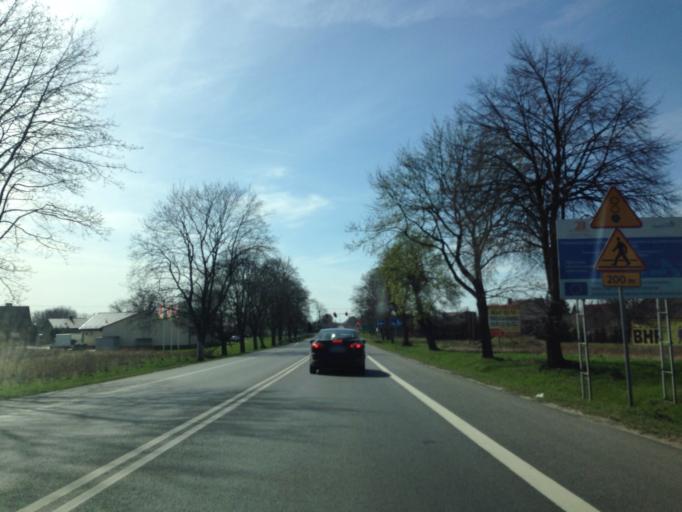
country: PL
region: Lodz Voivodeship
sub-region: Powiat sieradzki
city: Sieradz
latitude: 51.6015
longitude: 18.7916
